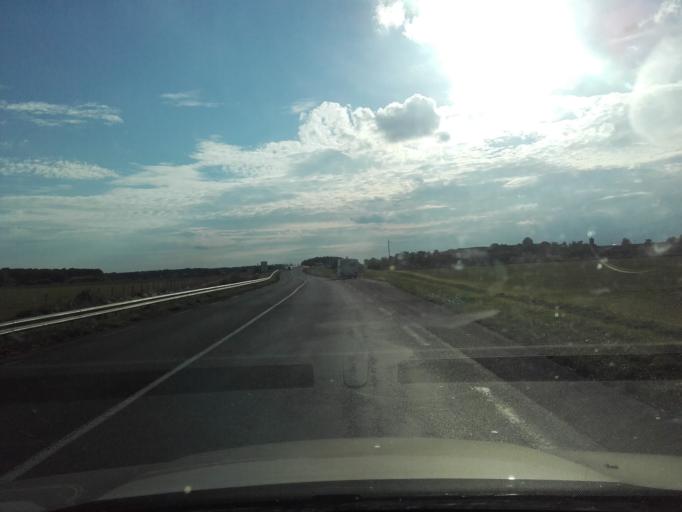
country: FR
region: Centre
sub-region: Departement d'Indre-et-Loire
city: Parcay-Meslay
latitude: 47.4769
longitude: 0.7599
